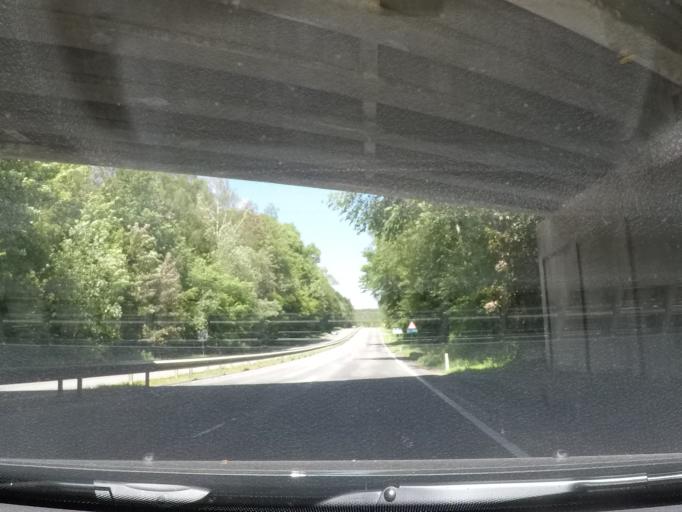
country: BE
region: Wallonia
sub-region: Province du Luxembourg
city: Saint-Hubert
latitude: 50.0275
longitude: 5.3839
